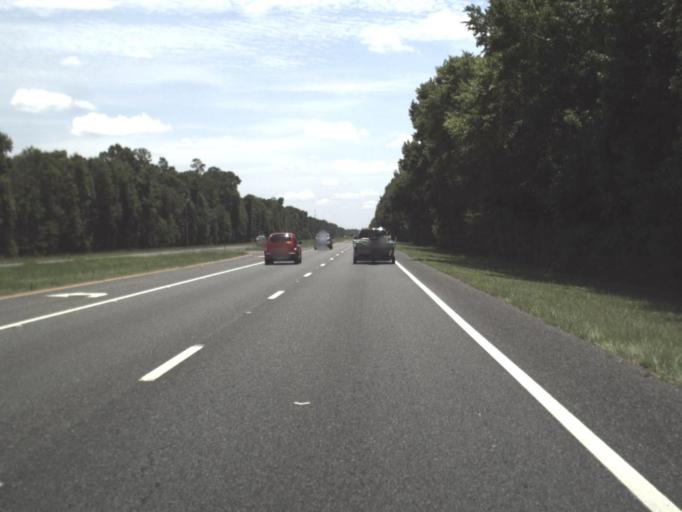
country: US
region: Florida
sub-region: Dixie County
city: Cross City
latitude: 29.6595
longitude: -83.1939
